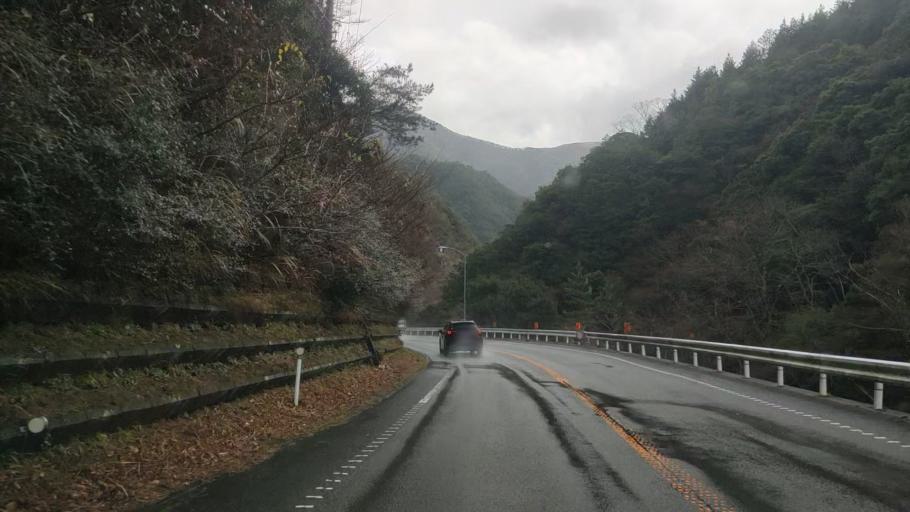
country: JP
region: Tokushima
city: Kamojimacho-jogejima
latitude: 34.1632
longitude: 134.3516
